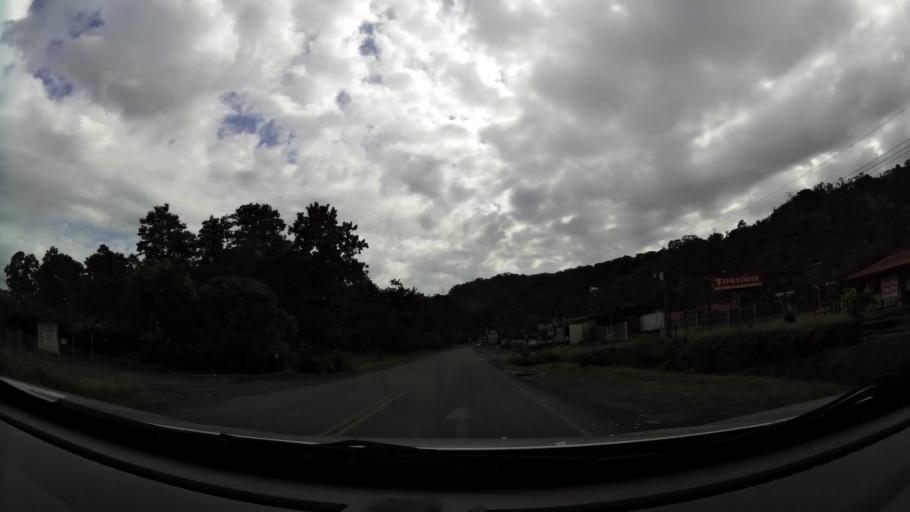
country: CR
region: Limon
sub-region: Canton de Siquirres
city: Siquirres
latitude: 10.0908
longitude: -83.4977
